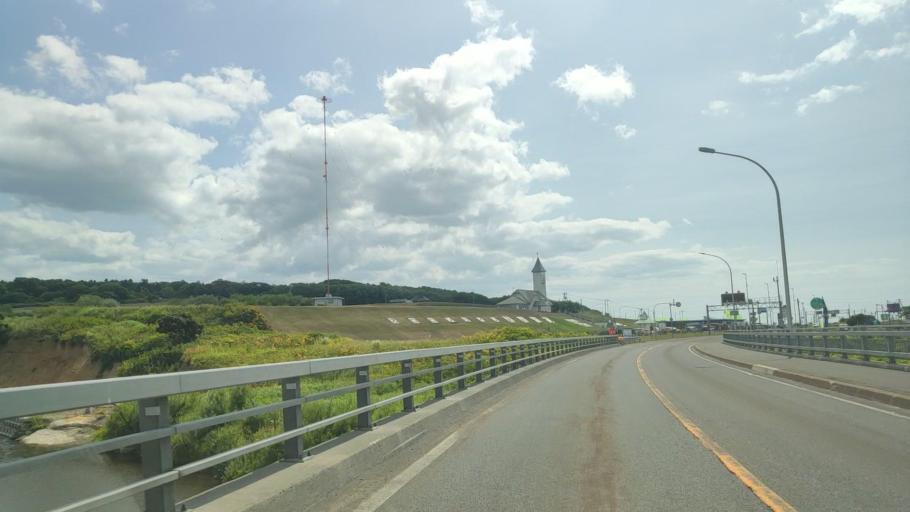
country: JP
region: Hokkaido
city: Makubetsu
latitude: 44.7168
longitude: 141.7932
